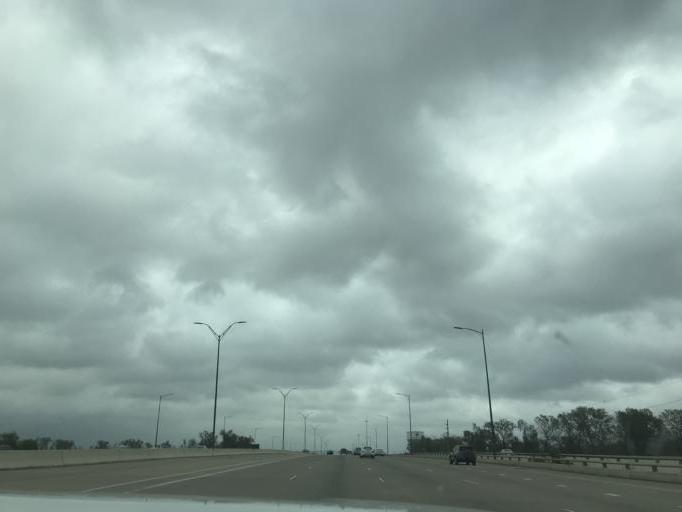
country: US
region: Texas
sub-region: Fort Bend County
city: Greatwood
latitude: 29.5671
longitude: -95.6696
